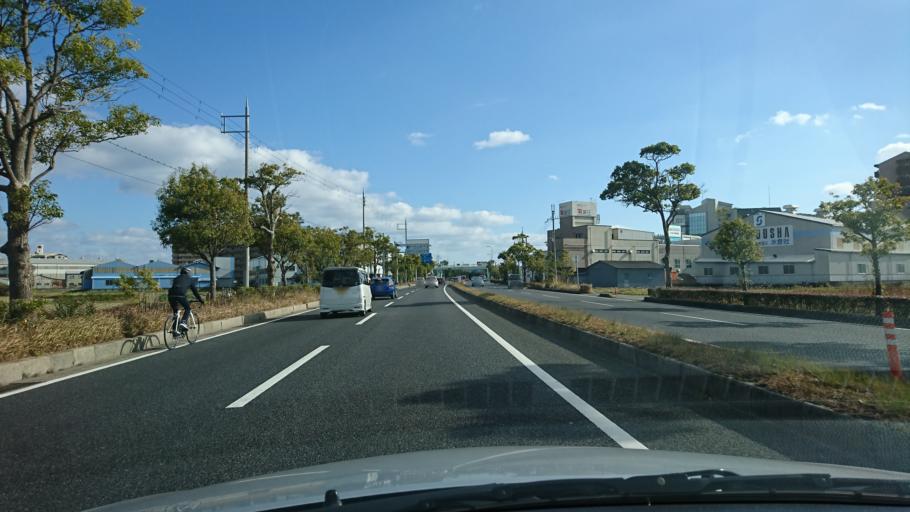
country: JP
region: Hyogo
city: Akashi
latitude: 34.6836
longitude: 134.9259
